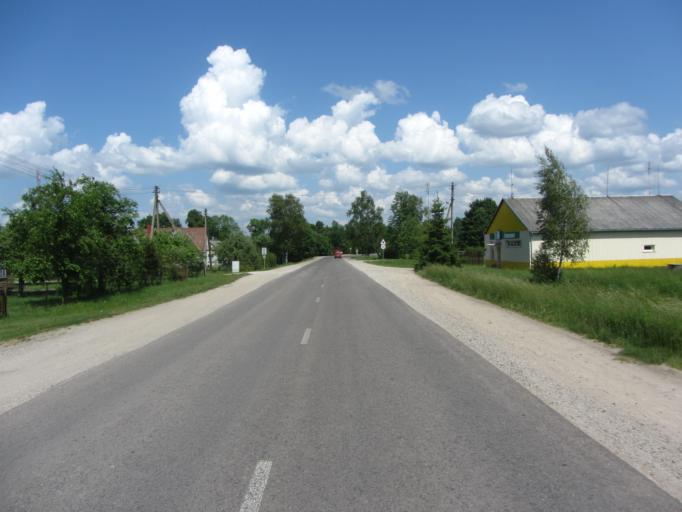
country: LT
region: Kauno apskritis
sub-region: Kauno rajonas
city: Karmelava
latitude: 54.8990
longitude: 24.2219
